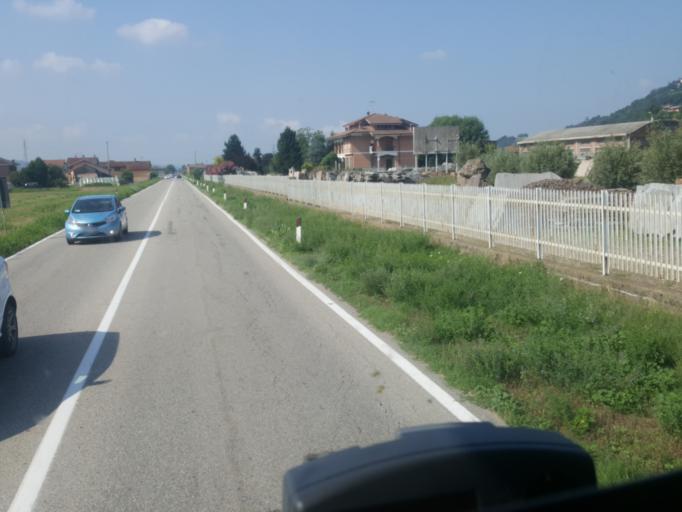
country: IT
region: Piedmont
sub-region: Provincia di Cuneo
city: Sant'Antonio
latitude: 44.7428
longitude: 8.0577
